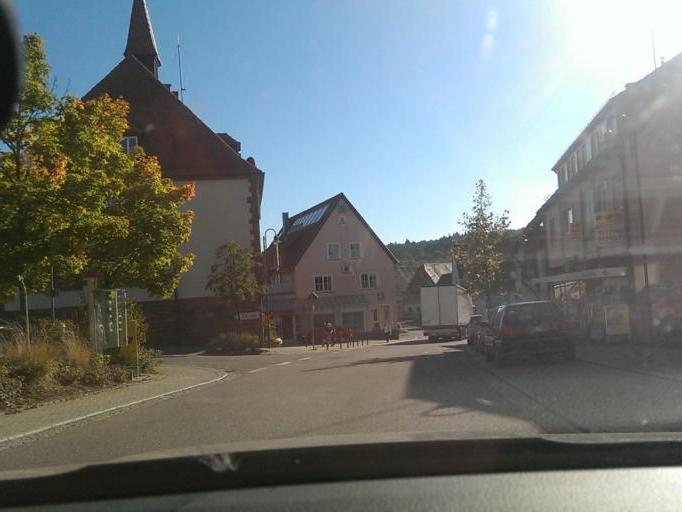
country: DE
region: Baden-Wuerttemberg
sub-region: Karlsruhe Region
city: Heimsheim
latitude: 48.8049
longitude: 8.8615
